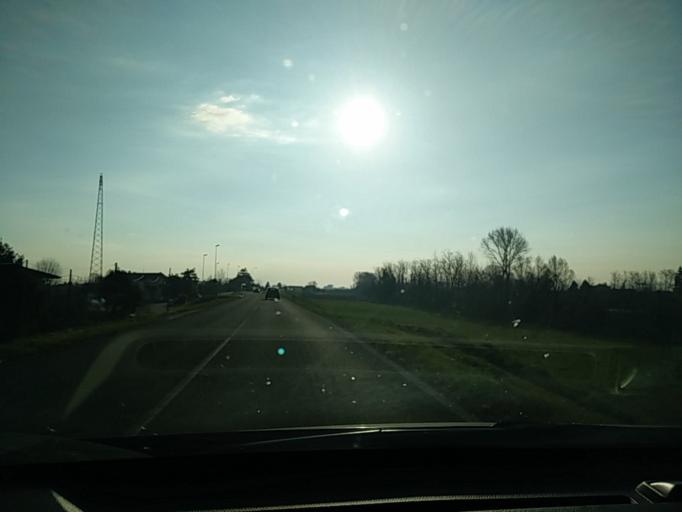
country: IT
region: Veneto
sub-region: Provincia di Venezia
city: Passarella
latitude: 45.5886
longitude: 12.6376
